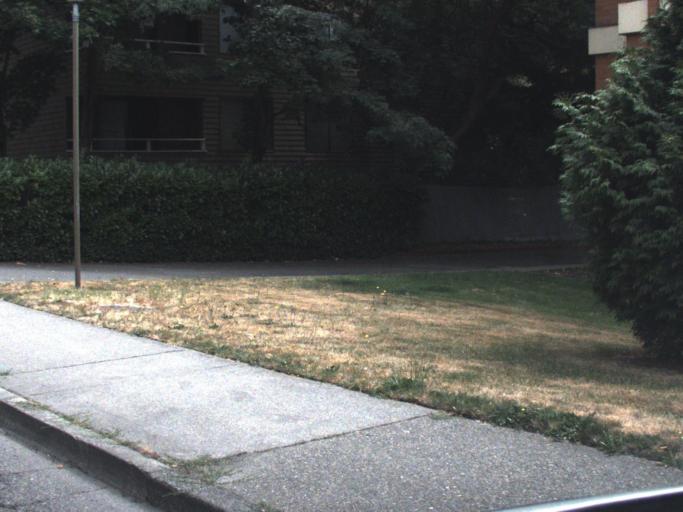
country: US
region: Washington
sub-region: King County
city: Lake Forest Park
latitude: 47.7338
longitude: -122.2954
